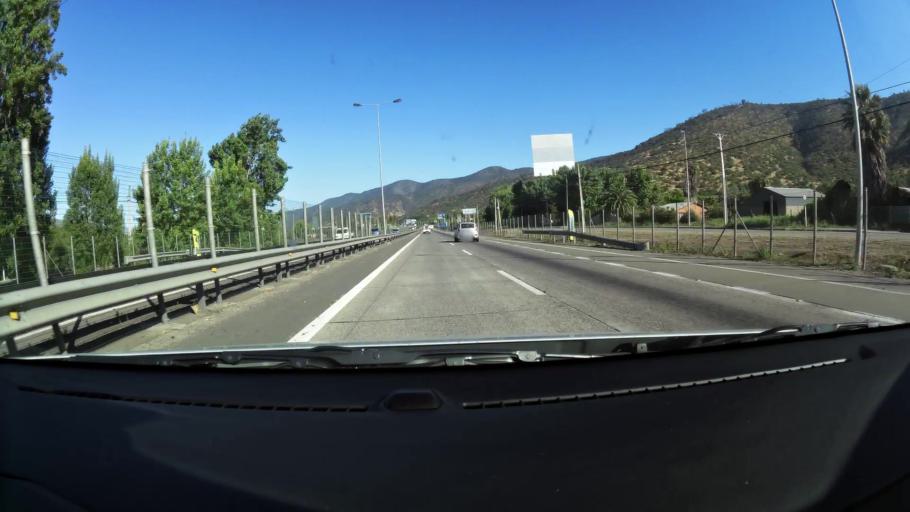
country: CL
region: Santiago Metropolitan
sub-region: Provincia de Chacabuco
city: Lampa
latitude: -33.4178
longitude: -71.0492
